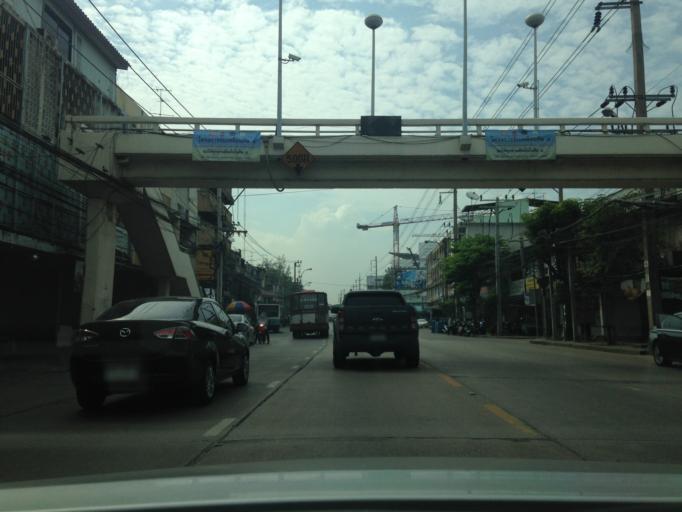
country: TH
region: Bangkok
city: Bang Sue
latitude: 13.8016
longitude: 100.5214
